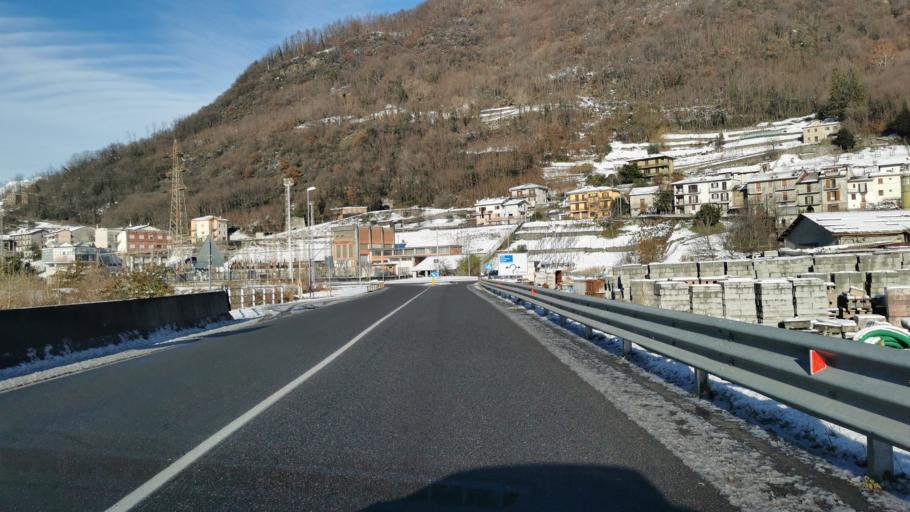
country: IT
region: Lombardy
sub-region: Provincia di Sondrio
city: Dubino
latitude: 46.1533
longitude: 9.4438
